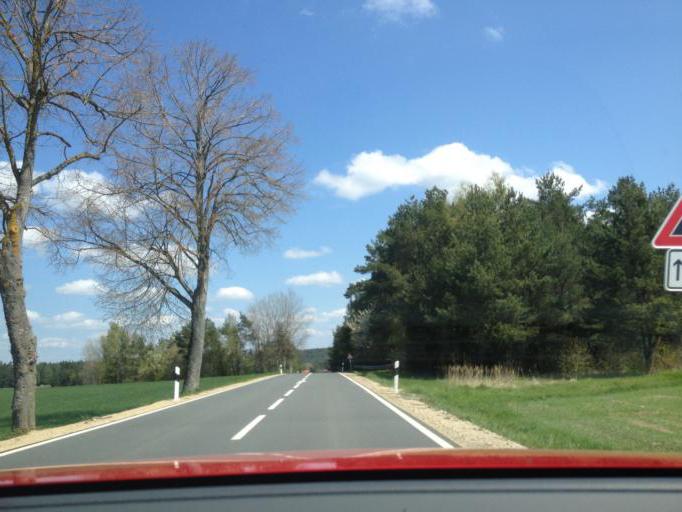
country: DE
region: Bavaria
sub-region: Upper Franconia
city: Pottenstein
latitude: 49.7169
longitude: 11.4474
